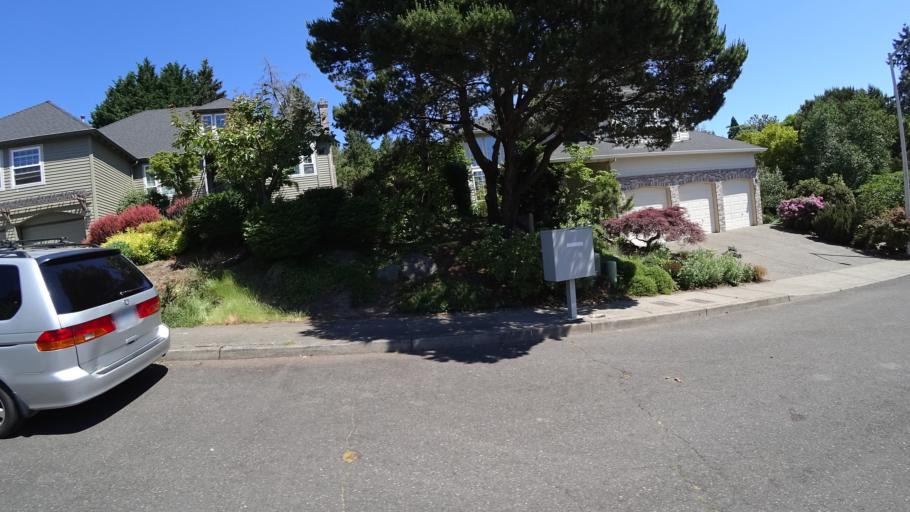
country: US
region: Oregon
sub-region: Washington County
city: Raleigh Hills
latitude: 45.4898
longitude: -122.7218
